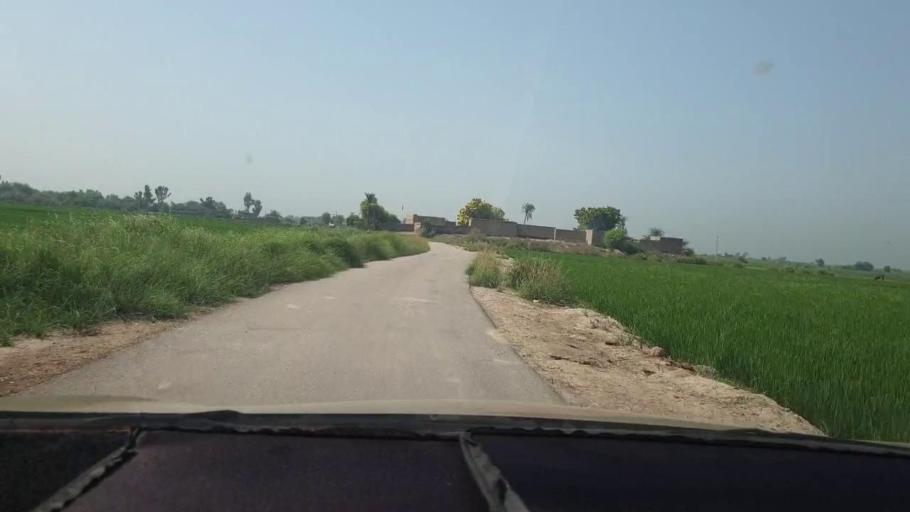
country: PK
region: Sindh
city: Kambar
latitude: 27.5623
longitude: 68.0442
